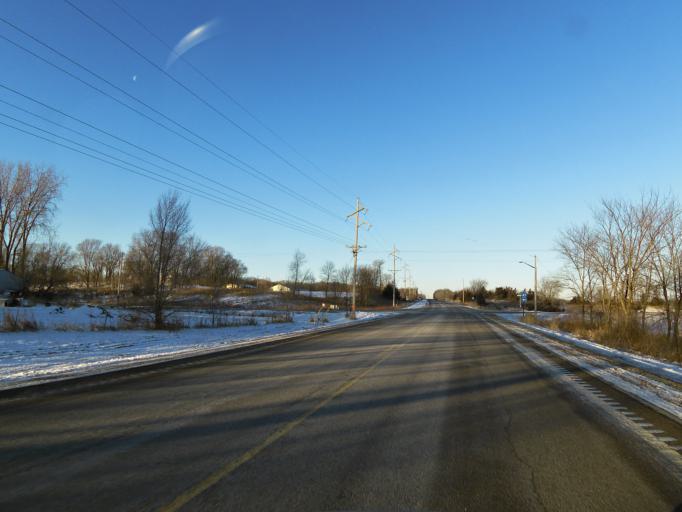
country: US
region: Minnesota
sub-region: Scott County
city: Prior Lake
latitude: 44.6746
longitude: -93.4184
